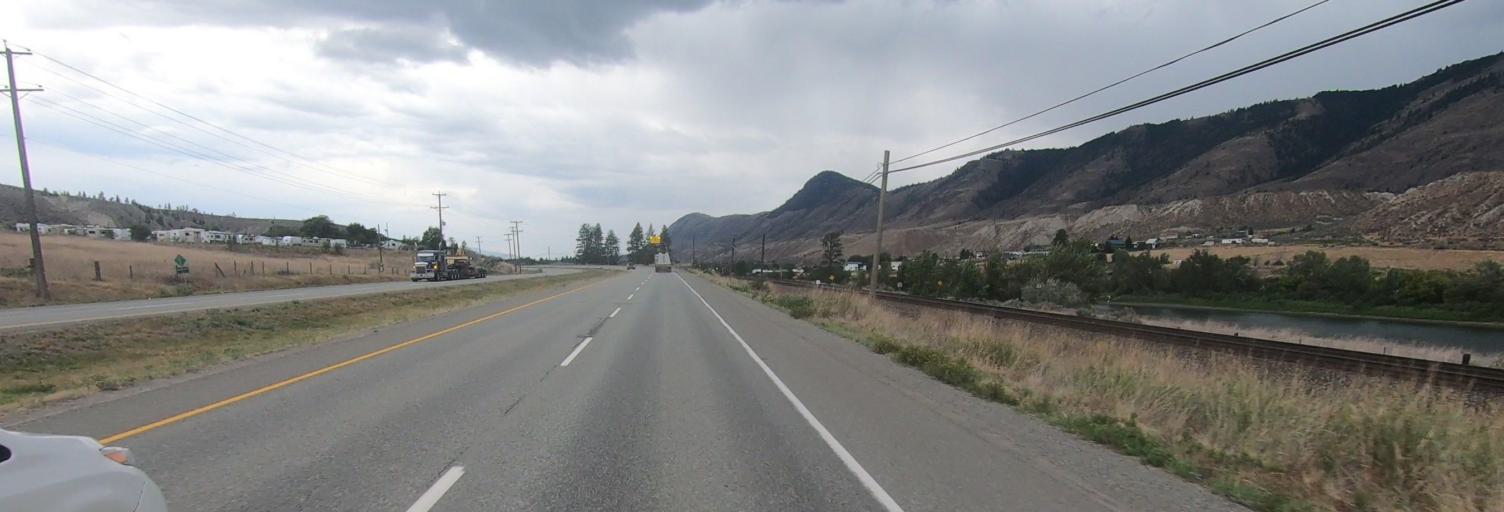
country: CA
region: British Columbia
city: Kamloops
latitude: 50.6712
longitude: -120.2096
